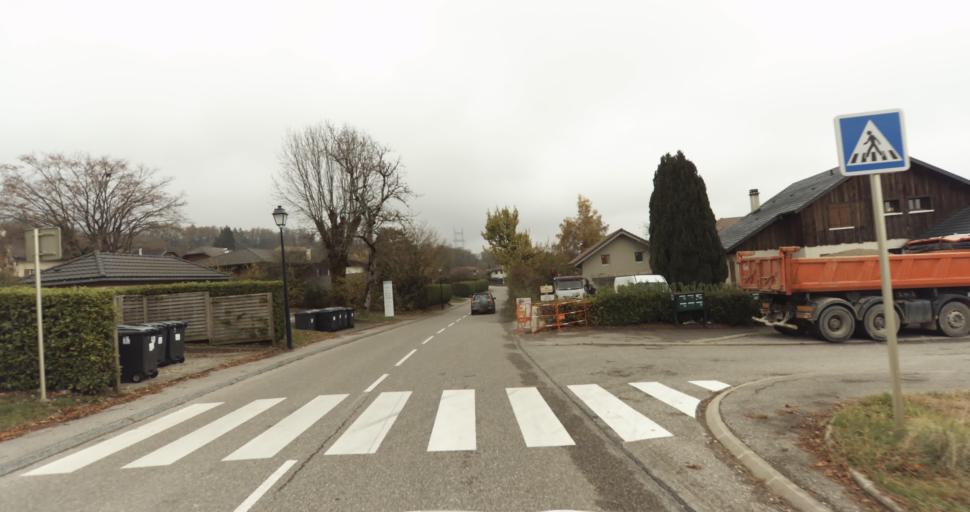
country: FR
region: Rhone-Alpes
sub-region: Departement de la Haute-Savoie
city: Viuz-la-Chiesaz
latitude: 45.8397
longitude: 6.0836
